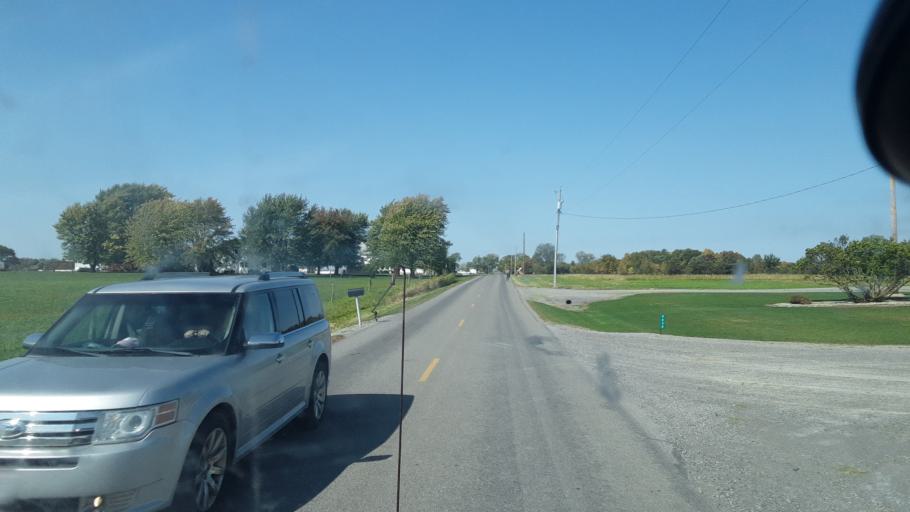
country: US
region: Ohio
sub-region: Logan County
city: Northwood
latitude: 40.4978
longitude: -83.7816
